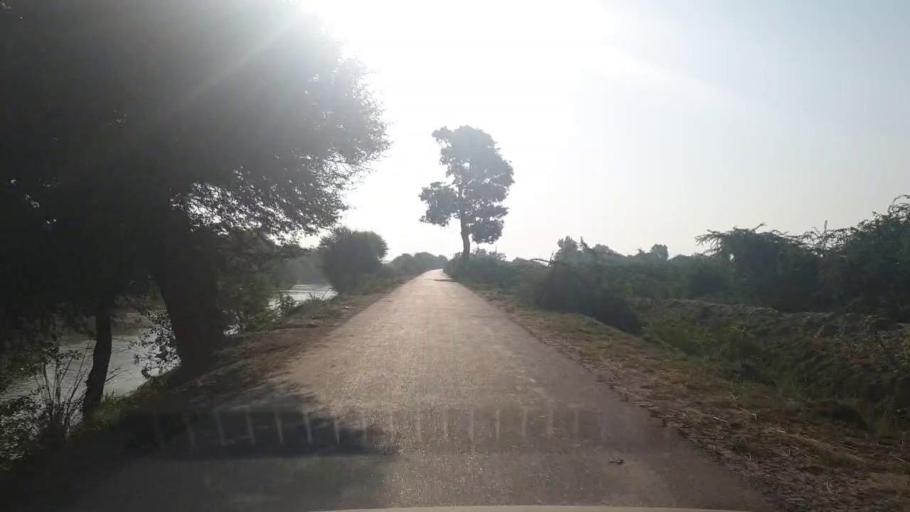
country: PK
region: Sindh
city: Tando Bago
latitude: 24.7340
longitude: 68.9325
